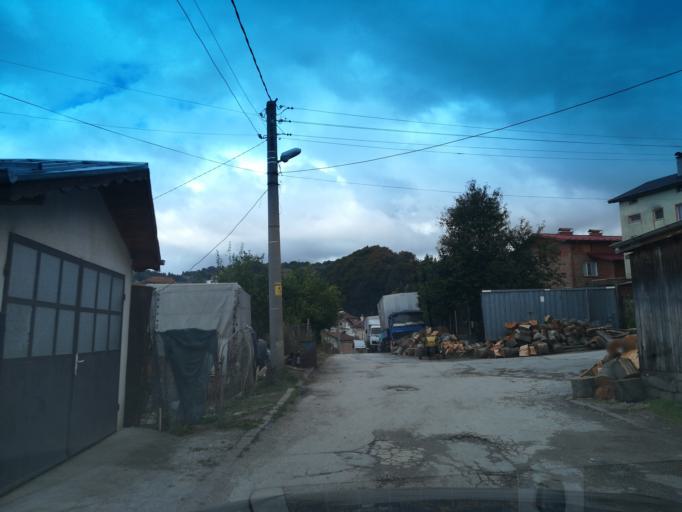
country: BG
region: Pazardzhik
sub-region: Obshtina Batak
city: Batak
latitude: 41.9371
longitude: 24.2669
